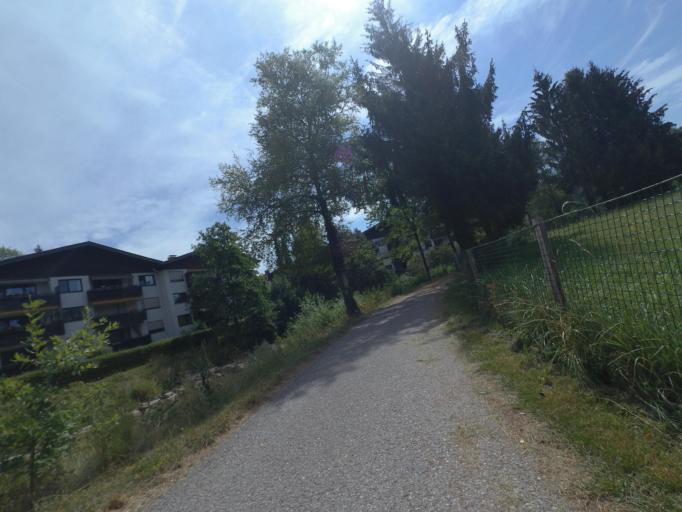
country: AT
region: Salzburg
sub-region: Politischer Bezirk Salzburg-Umgebung
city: Bergheim
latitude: 47.8467
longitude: 13.0404
